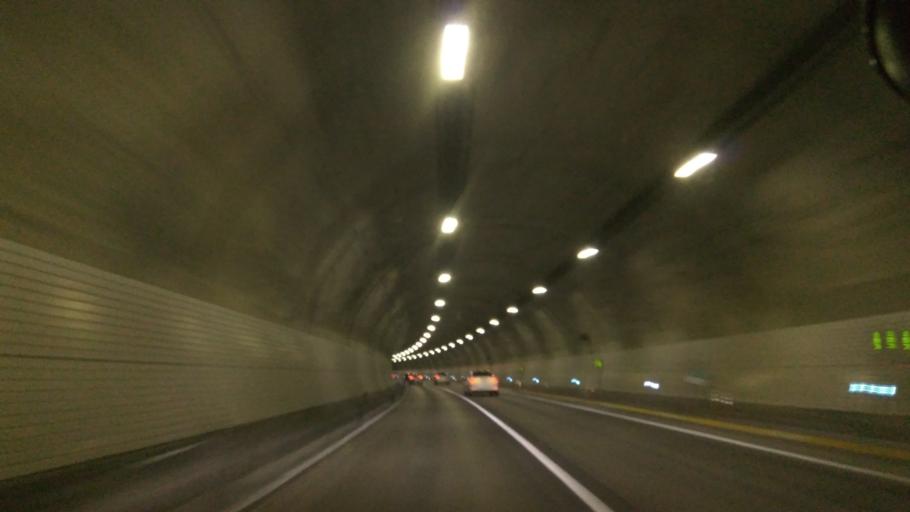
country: KR
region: Gyeonggi-do
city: Hwado
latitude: 37.6319
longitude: 127.3836
